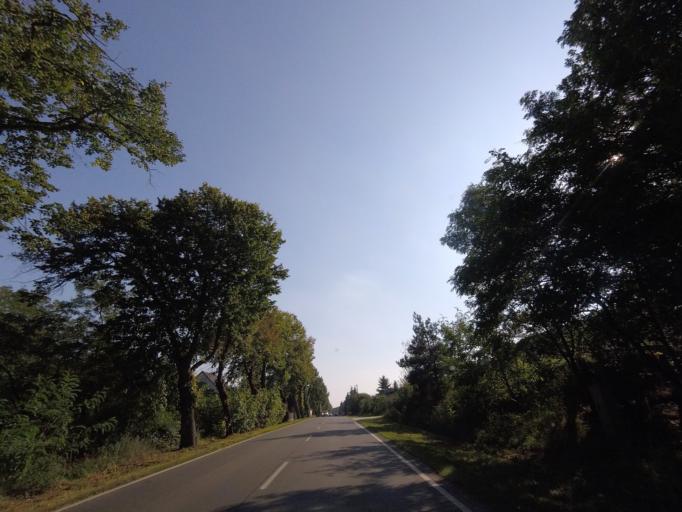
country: DE
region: Saxony-Anhalt
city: Jessen
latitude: 51.8027
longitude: 13.0162
